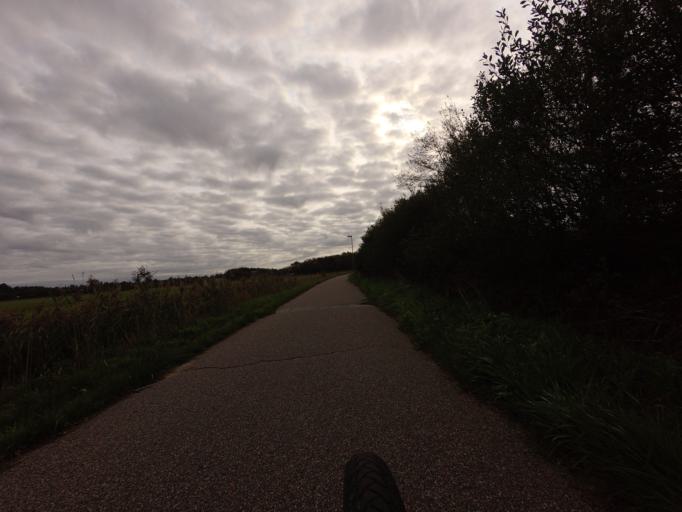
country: DK
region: North Denmark
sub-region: Hjorring Kommune
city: Hirtshals
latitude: 57.5641
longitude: 10.0200
